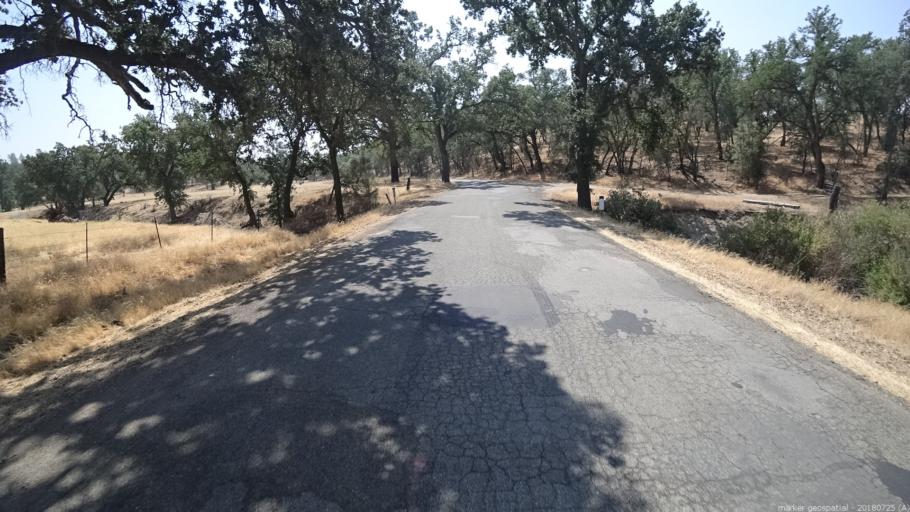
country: US
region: California
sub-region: San Luis Obispo County
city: Shandon
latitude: 35.8698
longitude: -120.4051
